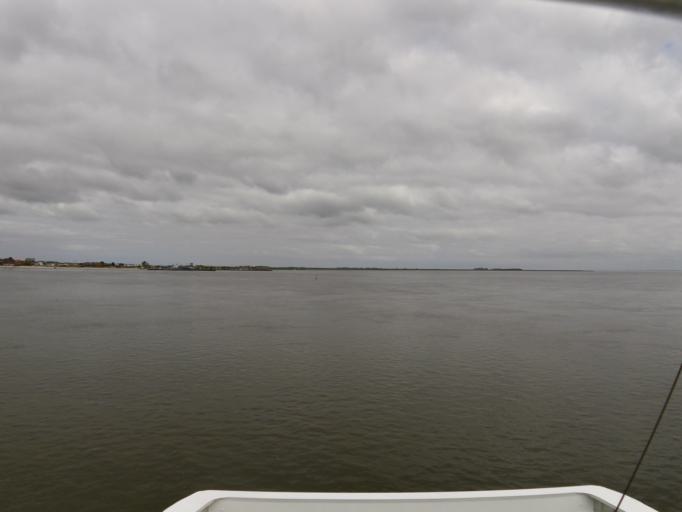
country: DE
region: Schleswig-Holstein
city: Wyk auf Fohr
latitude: 54.6843
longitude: 8.5881
